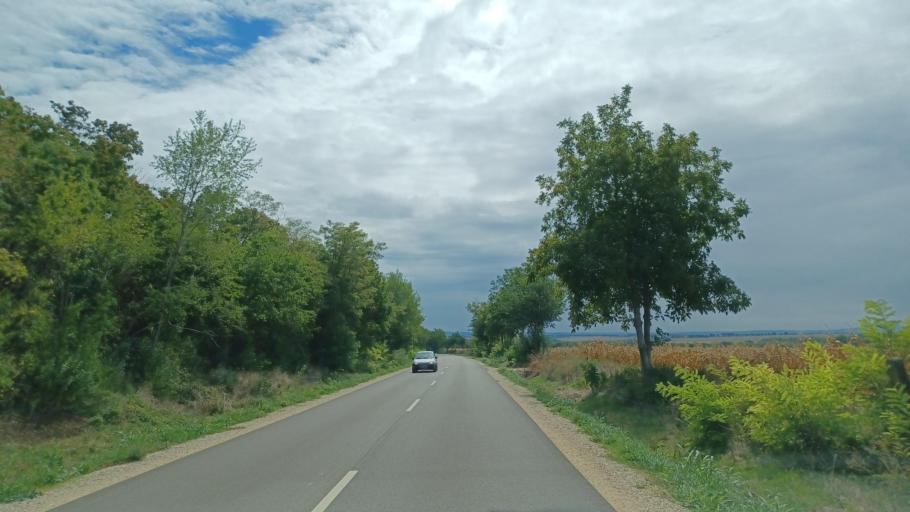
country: HU
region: Tolna
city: Zomba
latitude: 46.4676
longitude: 18.5962
